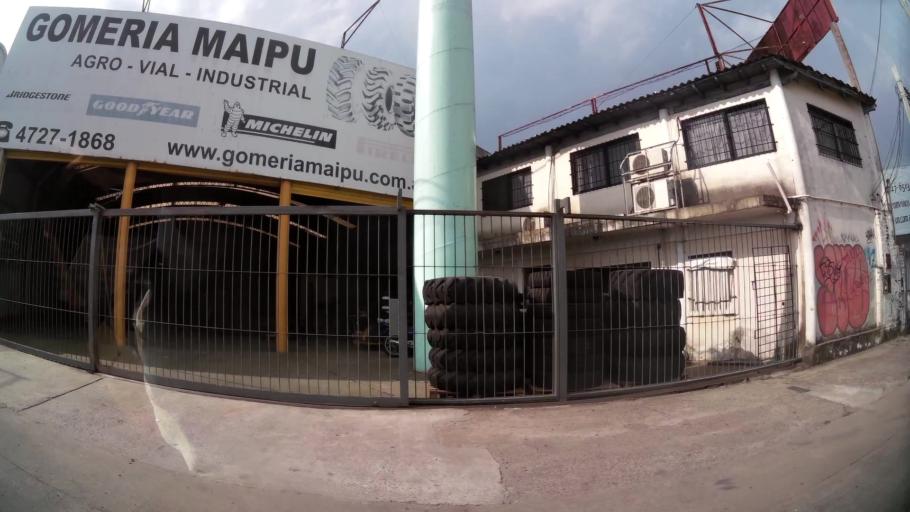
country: AR
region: Buenos Aires
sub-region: Partido de Tigre
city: Tigre
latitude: -34.4841
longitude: -58.6199
